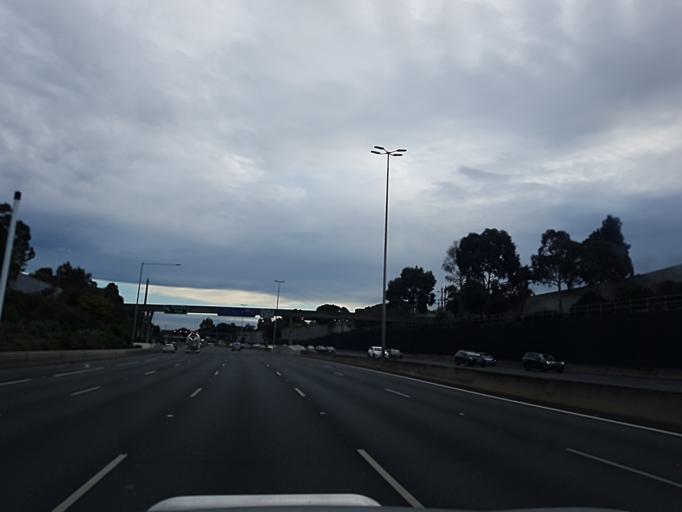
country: AU
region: Victoria
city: Brunswick West
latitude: -37.7571
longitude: 144.9376
